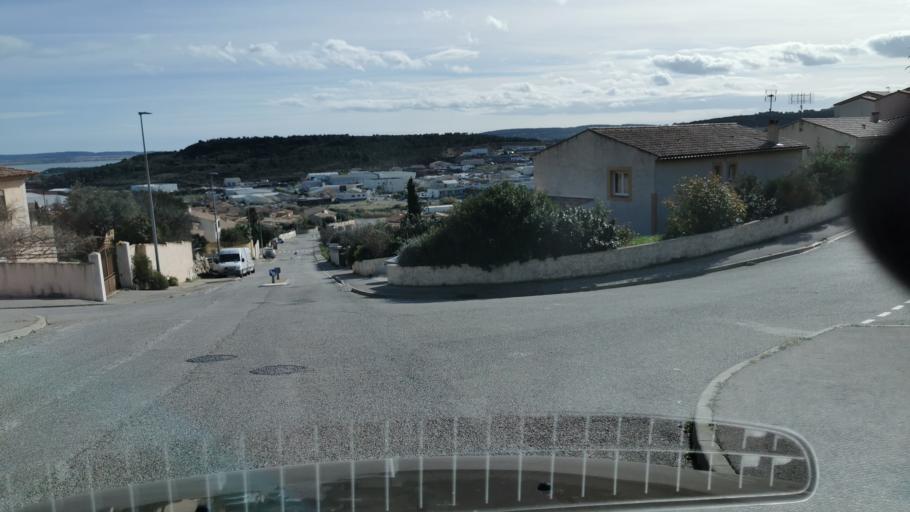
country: FR
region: Languedoc-Roussillon
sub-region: Departement de l'Aude
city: Narbonne
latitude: 43.1640
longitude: 2.9662
